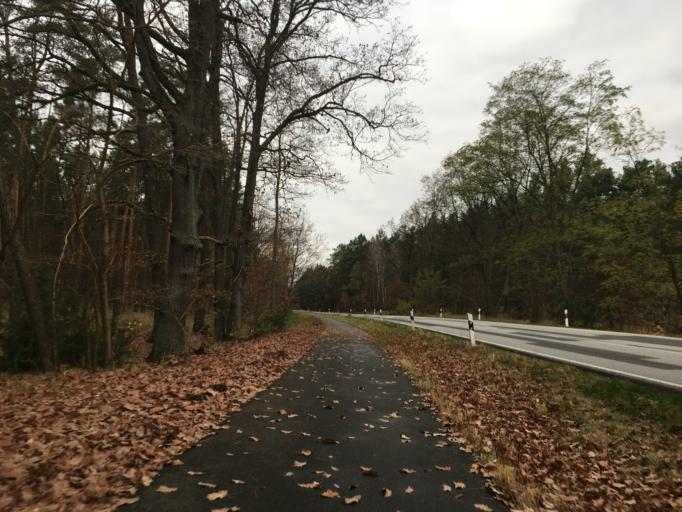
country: DE
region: Brandenburg
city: Mullrose
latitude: 52.2173
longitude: 14.4483
